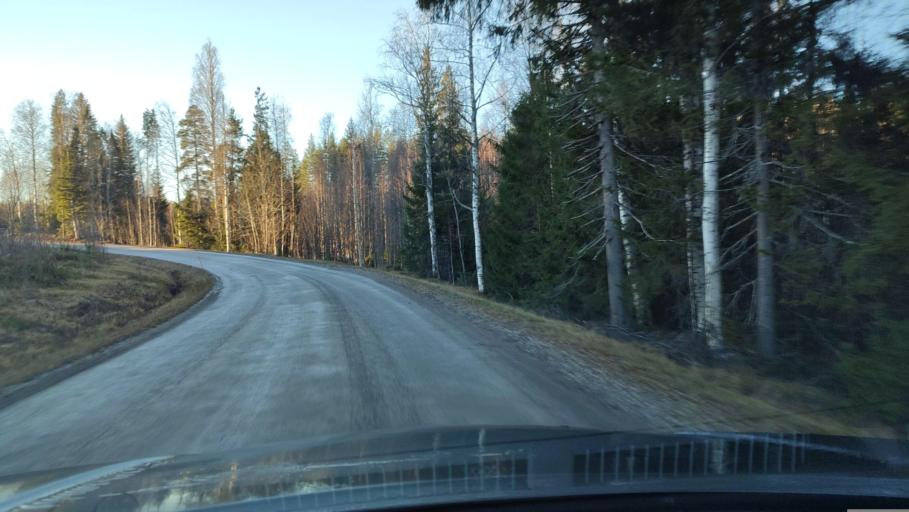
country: SE
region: Vaesterbotten
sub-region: Skelleftea Kommun
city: Viken
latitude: 64.7207
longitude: 20.9167
